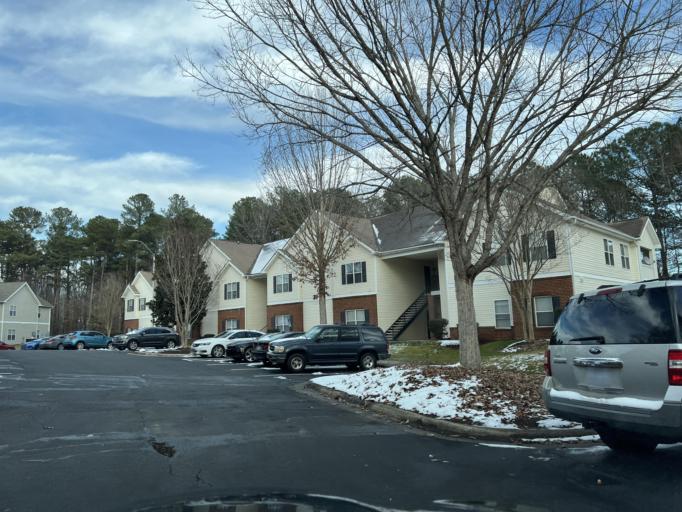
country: US
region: North Carolina
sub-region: Wake County
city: Raleigh
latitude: 35.8704
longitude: -78.5873
